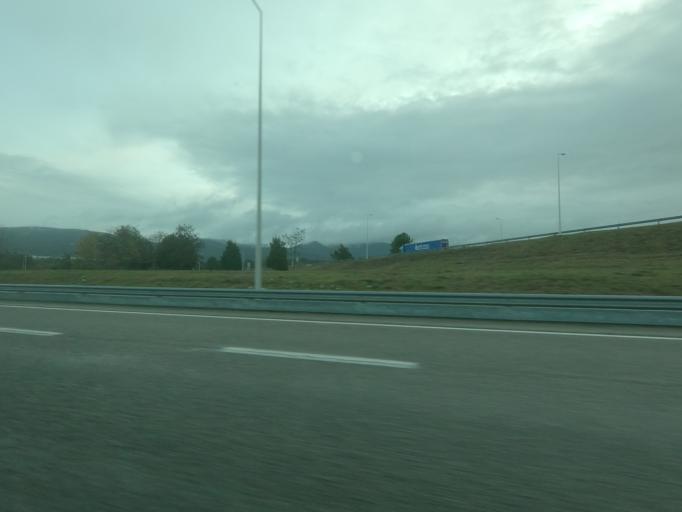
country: PT
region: Viana do Castelo
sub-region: Valenca
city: Valenza
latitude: 41.9878
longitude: -8.6461
